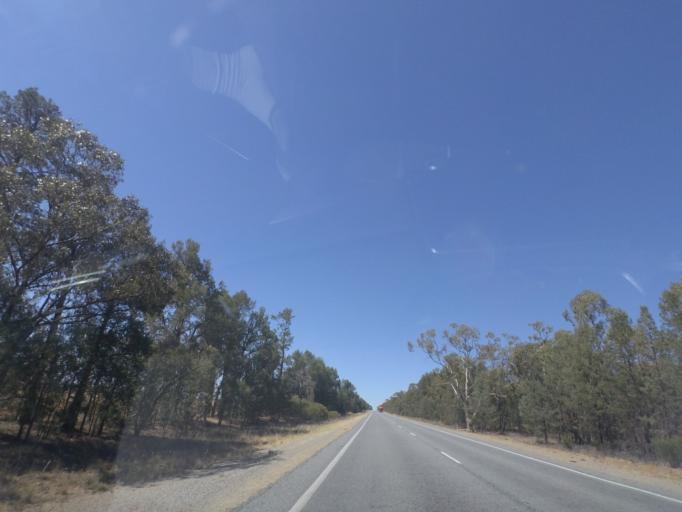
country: AU
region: New South Wales
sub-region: Narrandera
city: Narrandera
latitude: -34.4275
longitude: 146.8438
